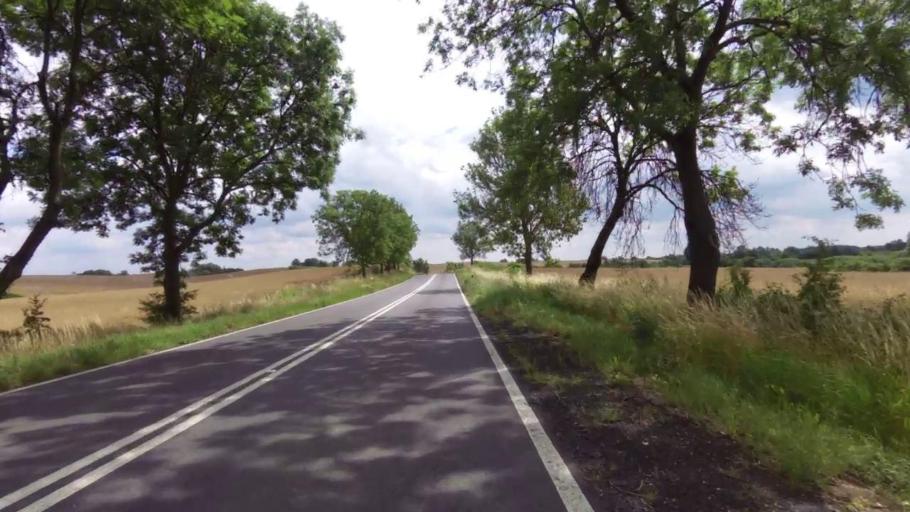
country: PL
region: West Pomeranian Voivodeship
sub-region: Powiat gryfinski
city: Moryn
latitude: 52.8718
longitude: 14.3443
